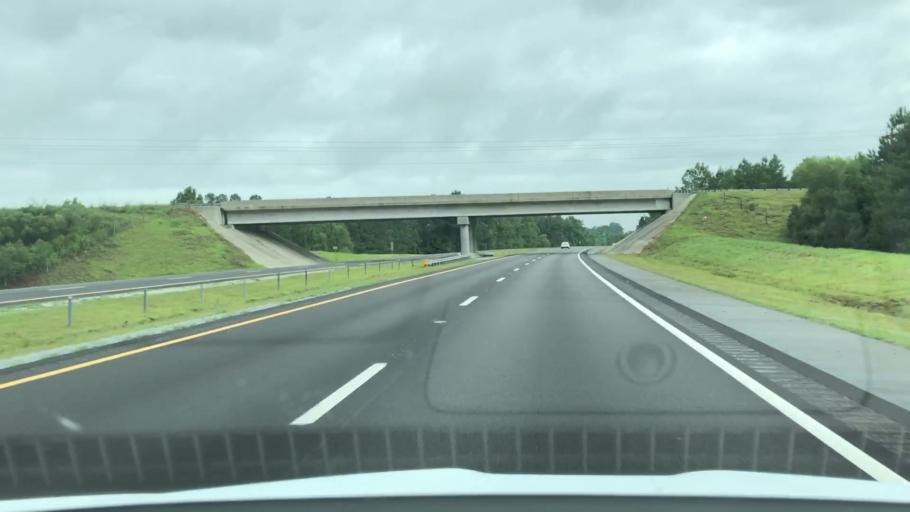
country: US
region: North Carolina
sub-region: Wayne County
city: Fremont
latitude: 35.5384
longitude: -77.9901
